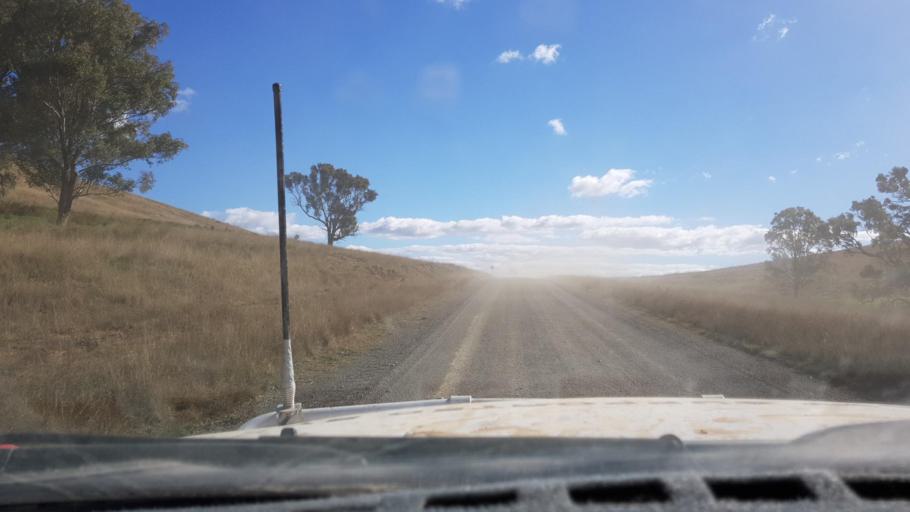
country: AU
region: New South Wales
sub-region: Narrabri
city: Blair Athol
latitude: -30.4790
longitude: 150.4369
